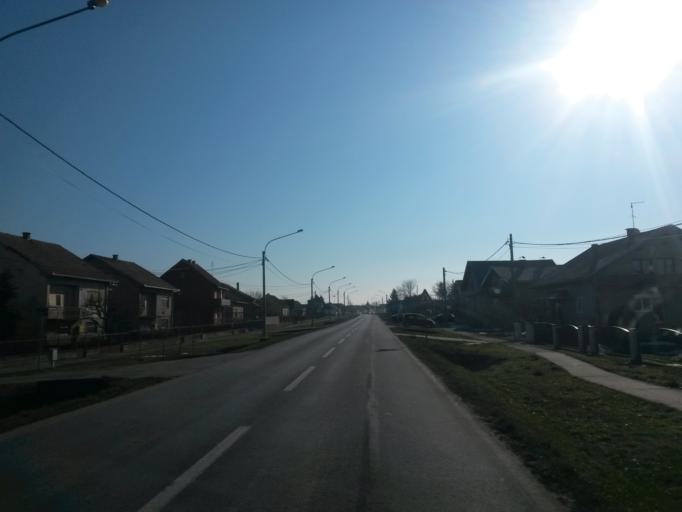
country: HR
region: Osjecko-Baranjska
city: Sarvas
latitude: 45.5287
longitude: 18.8312
